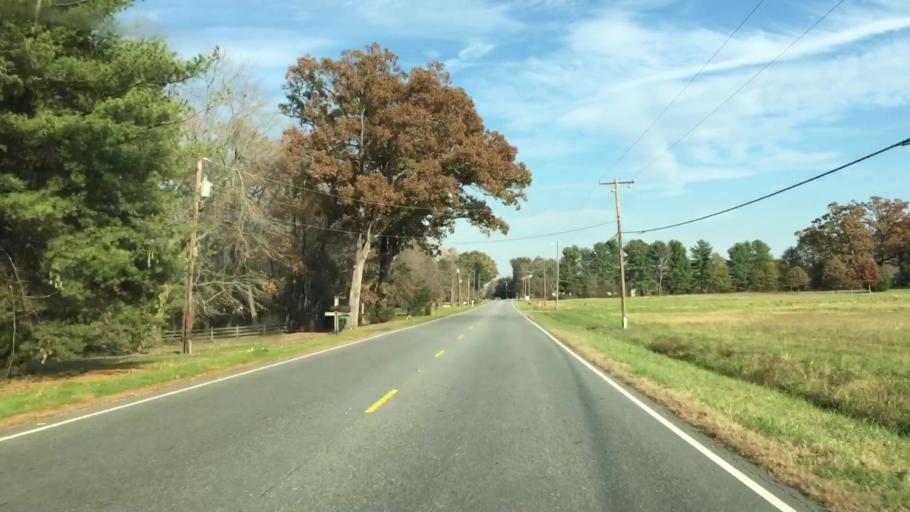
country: US
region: North Carolina
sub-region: Guilford County
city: Summerfield
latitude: 36.2565
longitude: -79.8814
